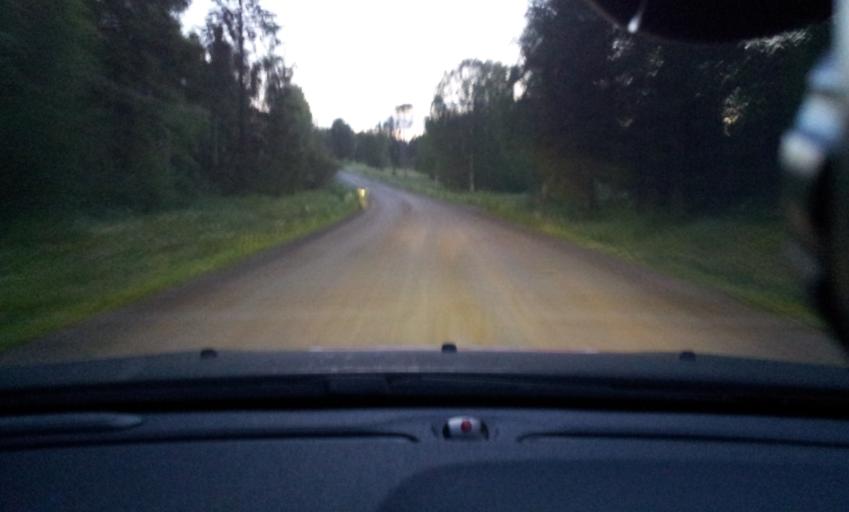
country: SE
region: Jaemtland
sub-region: Braecke Kommun
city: Braecke
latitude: 62.7283
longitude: 15.4928
